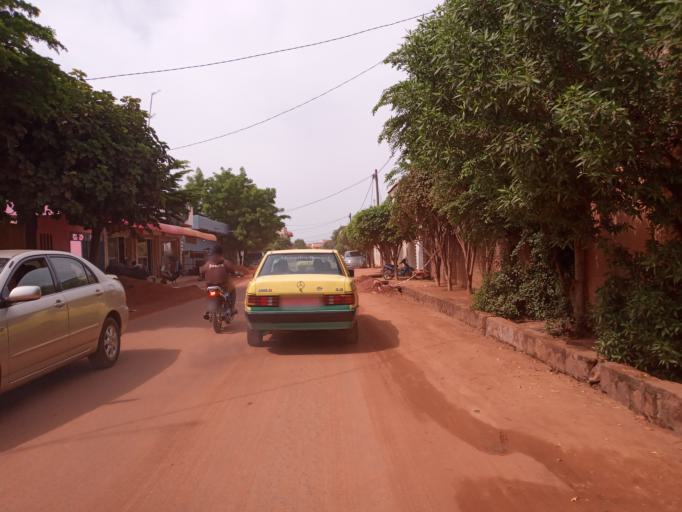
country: ML
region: Bamako
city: Bamako
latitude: 12.5636
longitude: -7.9901
